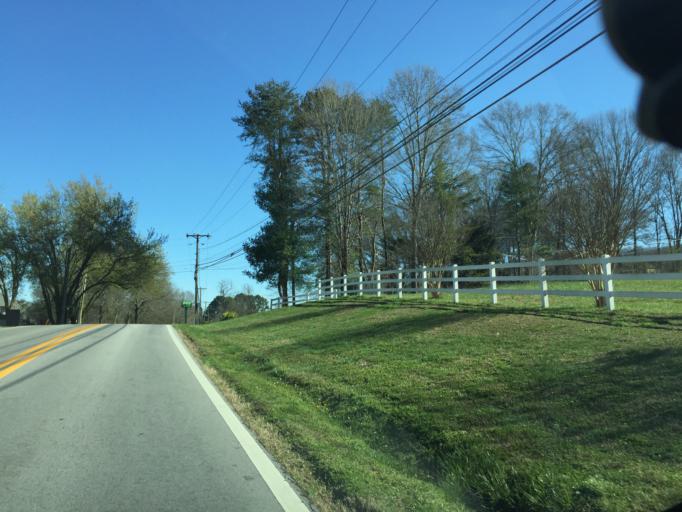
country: US
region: Tennessee
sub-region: Hamilton County
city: Middle Valley
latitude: 35.1344
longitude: -85.2110
